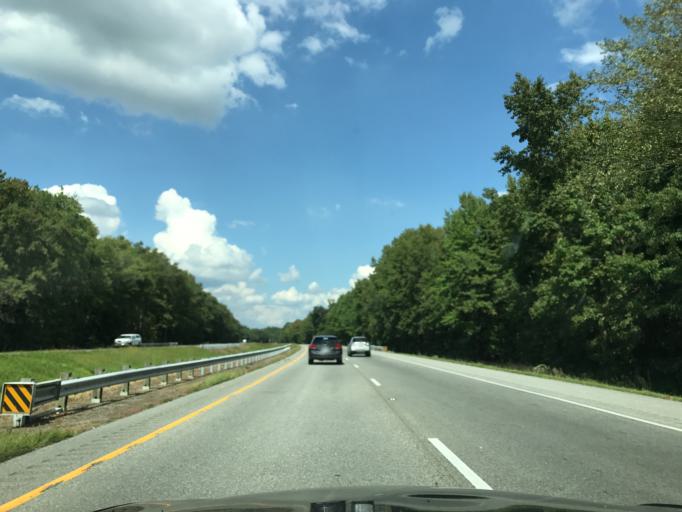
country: US
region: Maryland
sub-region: Queen Anne's County
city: Kingstown
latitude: 39.2297
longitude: -75.8749
